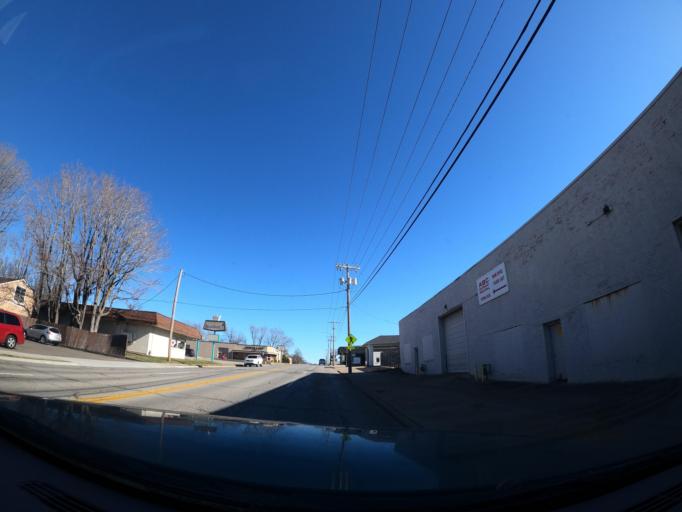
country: US
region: Oklahoma
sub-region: Tulsa County
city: Tulsa
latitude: 36.1405
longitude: -95.9479
